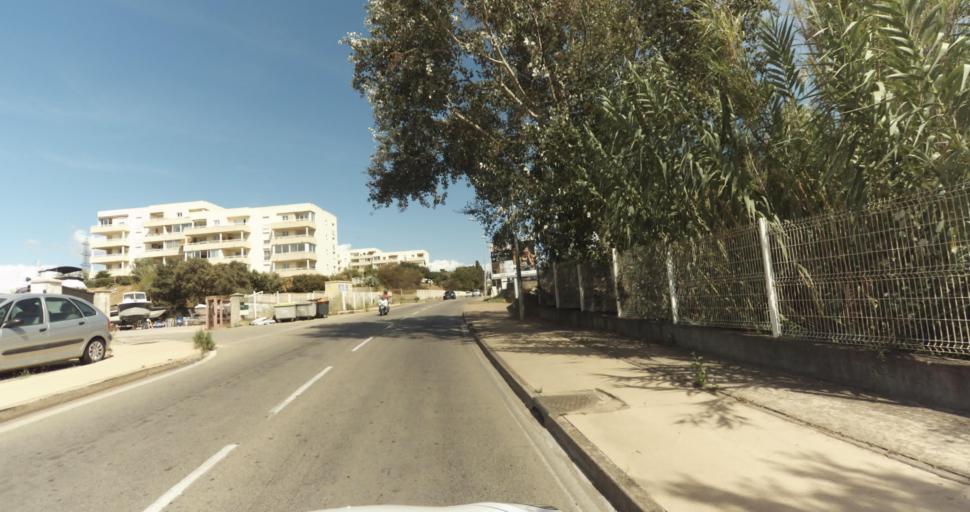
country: FR
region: Corsica
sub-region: Departement de la Corse-du-Sud
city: Ajaccio
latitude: 41.9465
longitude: 8.7612
